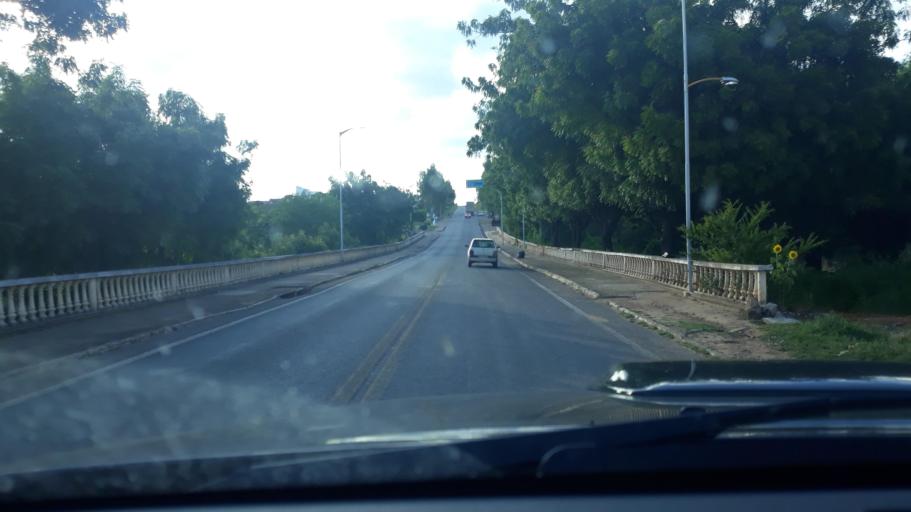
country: BR
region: Bahia
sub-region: Riacho De Santana
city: Riacho de Santana
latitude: -13.7682
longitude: -42.7192
